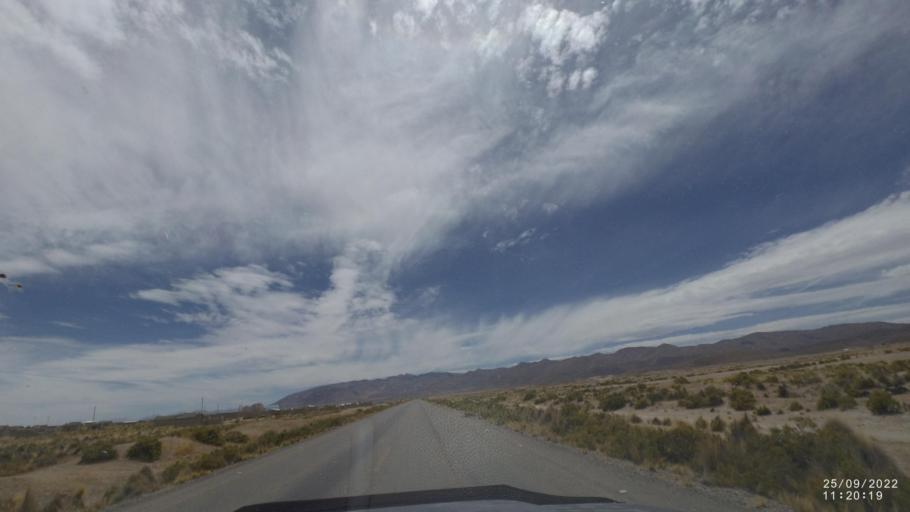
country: BO
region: Oruro
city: Challapata
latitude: -19.1611
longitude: -66.7768
